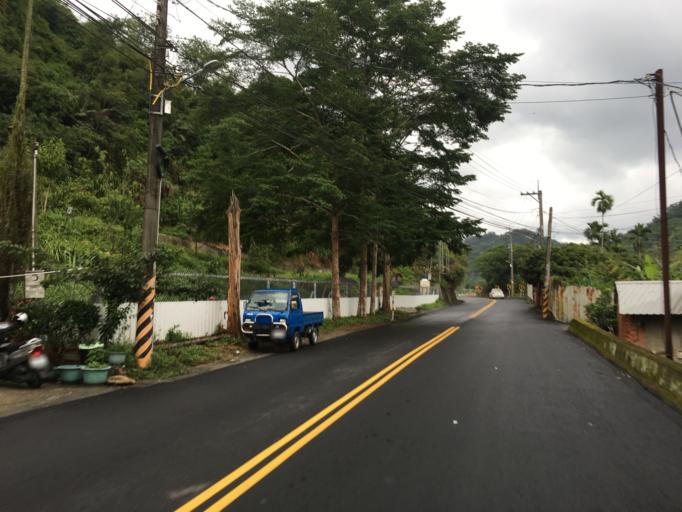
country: TW
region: Taiwan
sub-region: Taichung City
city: Taichung
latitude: 24.0687
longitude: 120.7338
